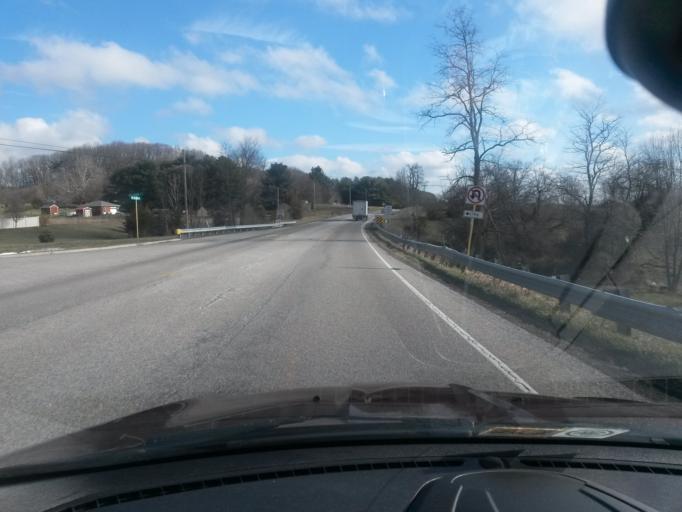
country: US
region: Virginia
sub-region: Augusta County
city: Jolivue
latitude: 38.0333
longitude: -79.1375
